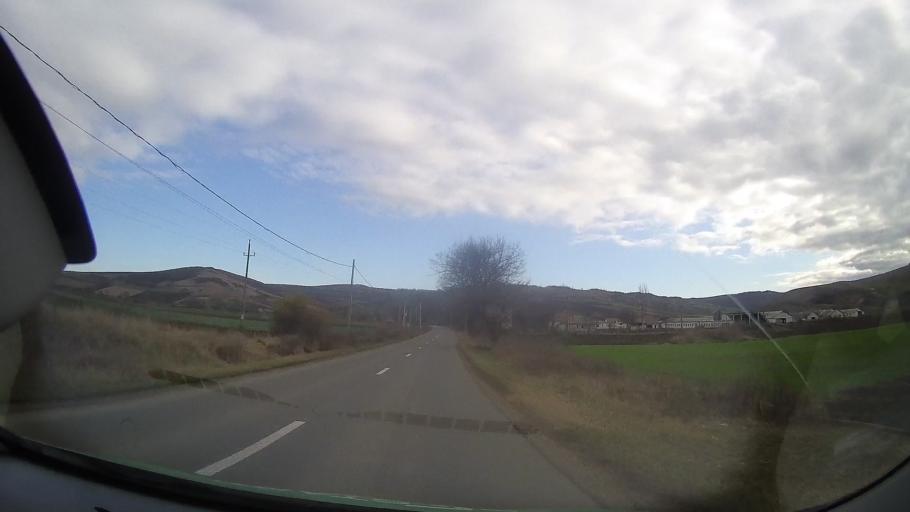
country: RO
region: Mures
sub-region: Comuna Iernut
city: Iernut
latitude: 46.4894
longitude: 24.2519
